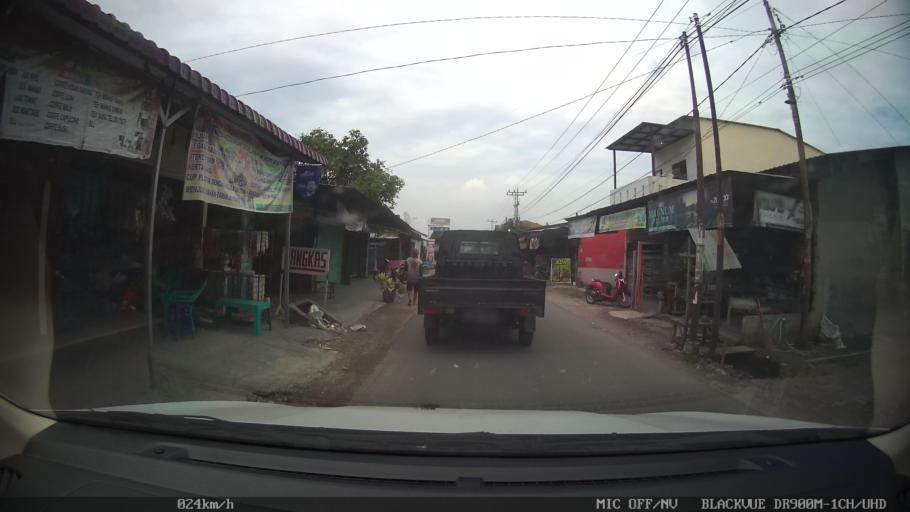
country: ID
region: North Sumatra
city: Binjai
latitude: 3.6292
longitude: 98.5556
